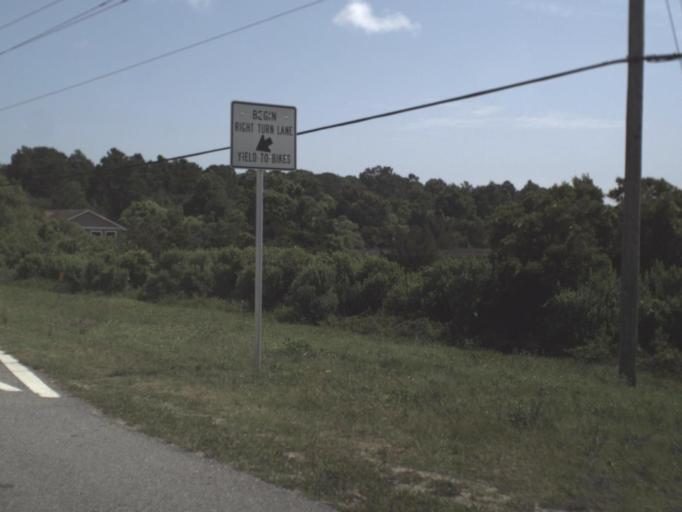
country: US
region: Florida
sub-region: Saint Johns County
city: Saint Augustine Shores
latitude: 29.8227
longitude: -81.3223
